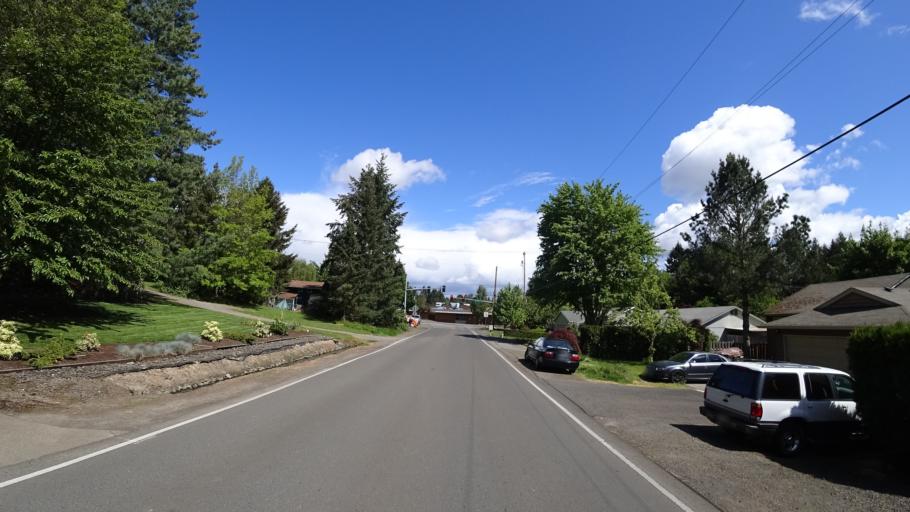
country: US
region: Oregon
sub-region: Washington County
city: Aloha
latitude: 45.4743
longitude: -122.8375
